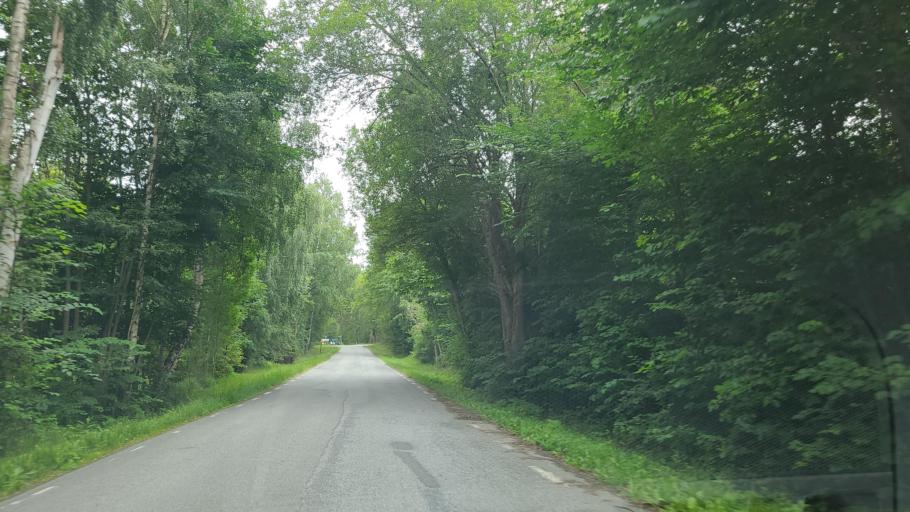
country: SE
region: Stockholm
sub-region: Upplands-Bro Kommun
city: Bro
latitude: 59.4899
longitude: 17.5670
